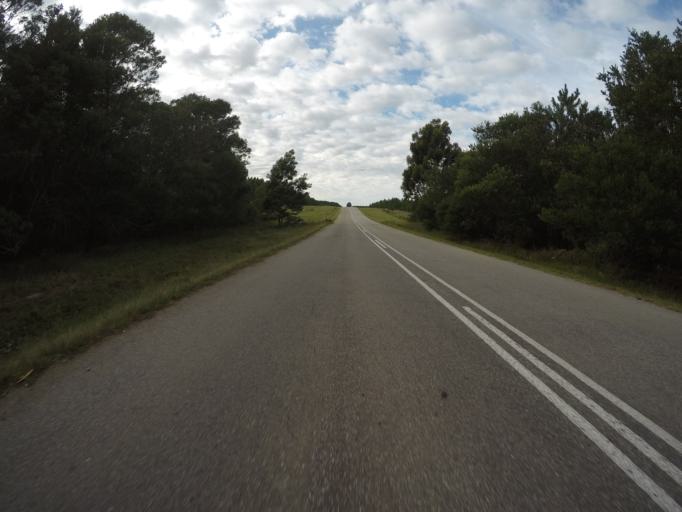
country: ZA
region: Eastern Cape
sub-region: Cacadu District Municipality
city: Kareedouw
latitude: -34.0244
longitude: 24.3650
